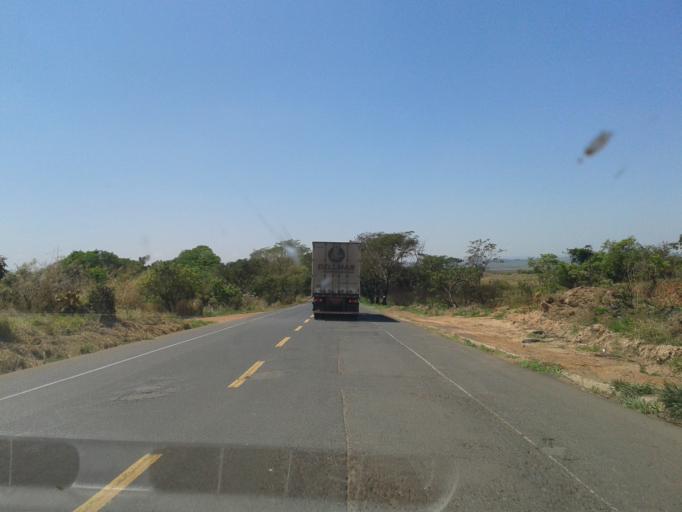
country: BR
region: Minas Gerais
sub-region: Araxa
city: Araxa
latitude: -19.4314
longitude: -47.2238
